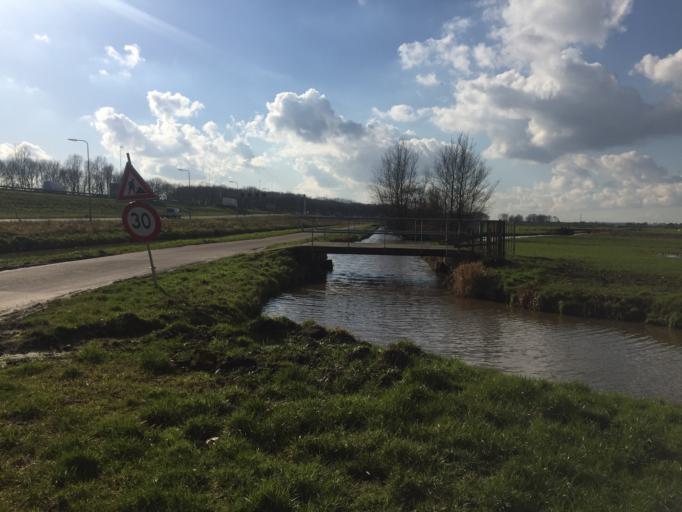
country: NL
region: Utrecht
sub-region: Gemeente Oudewater
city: Oudewater
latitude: 52.0669
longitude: 4.8220
